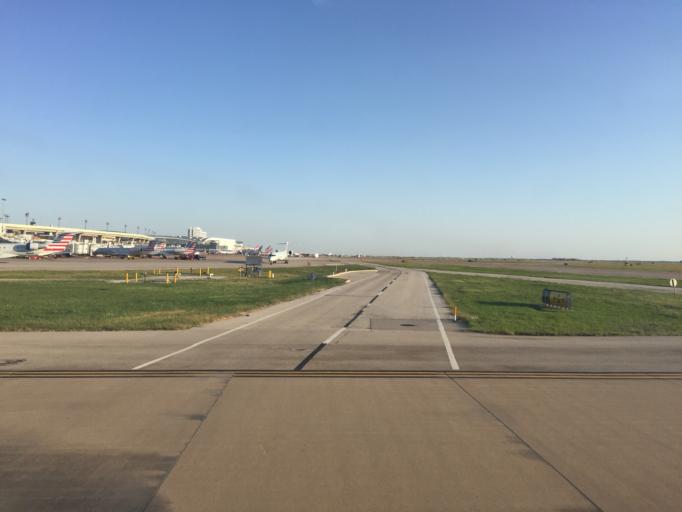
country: US
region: Texas
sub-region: Tarrant County
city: Grapevine
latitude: 32.9090
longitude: -97.0468
